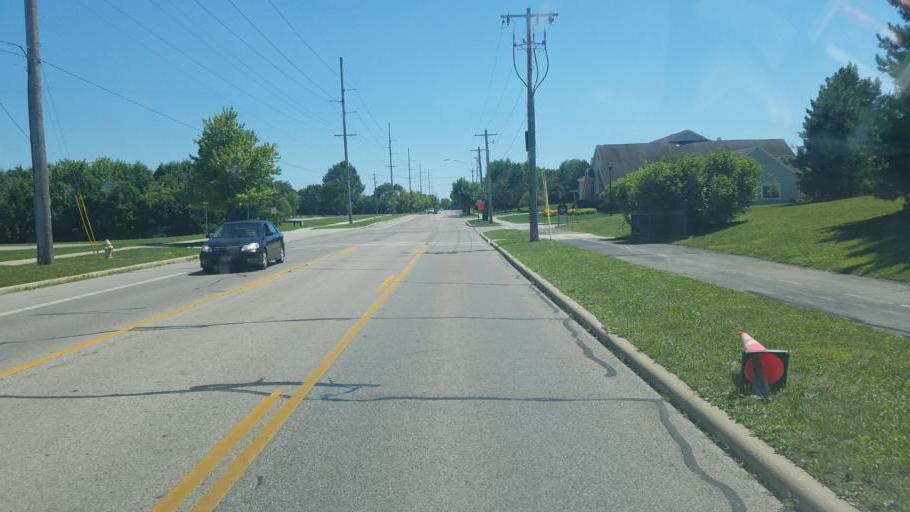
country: US
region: Ohio
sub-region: Franklin County
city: Westerville
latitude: 40.1359
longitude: -82.9026
